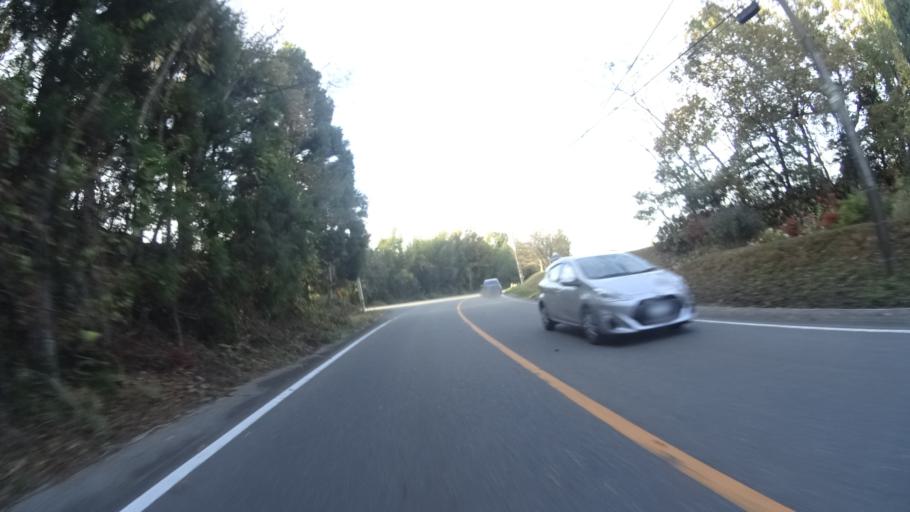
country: JP
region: Ishikawa
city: Nanao
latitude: 37.1697
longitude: 136.7141
